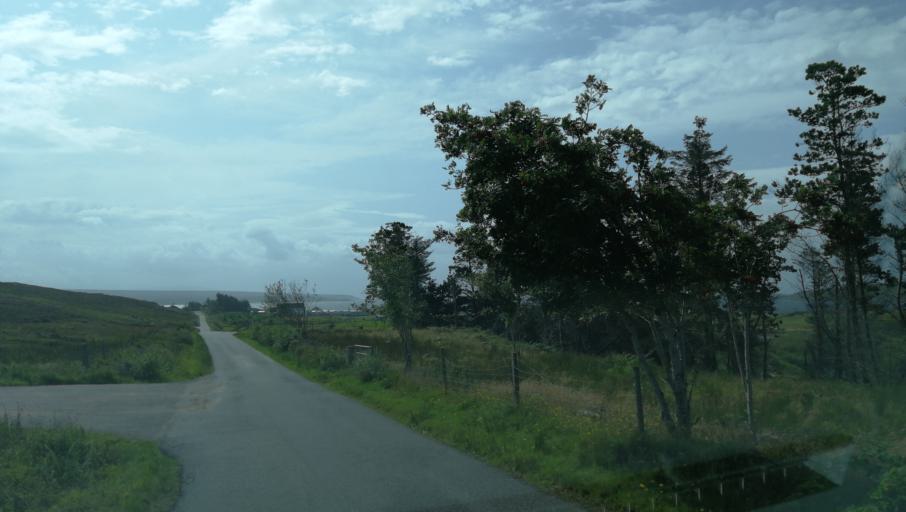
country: GB
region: Scotland
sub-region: Highland
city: Portree
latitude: 57.7454
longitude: -5.7632
